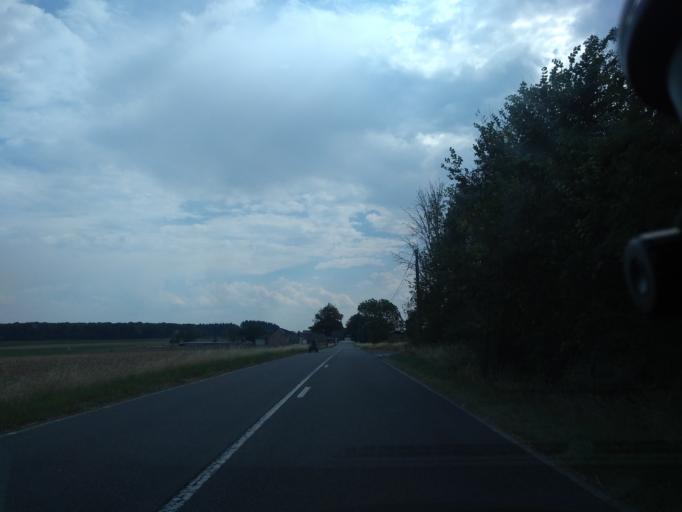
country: BE
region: Wallonia
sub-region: Province de Namur
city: Dinant
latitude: 50.1884
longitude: 4.8992
